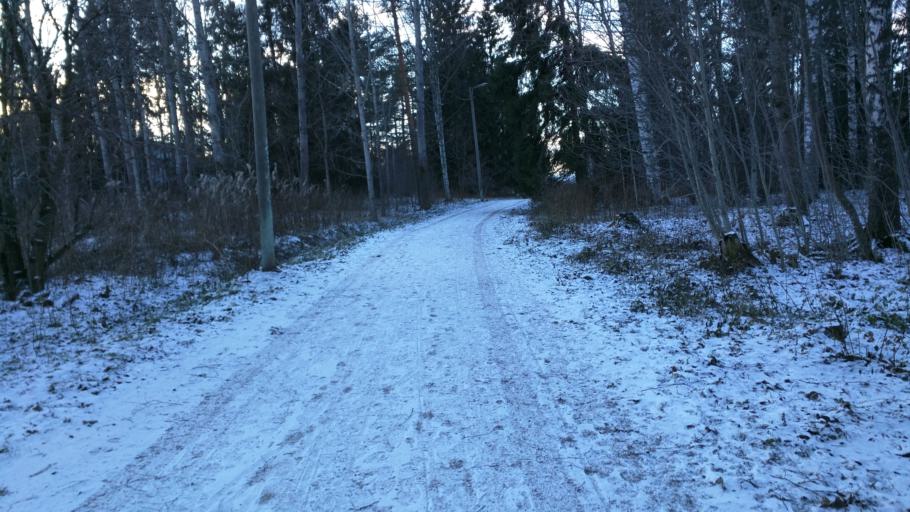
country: FI
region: Uusimaa
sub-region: Helsinki
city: Kauniainen
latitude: 60.2416
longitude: 24.7518
